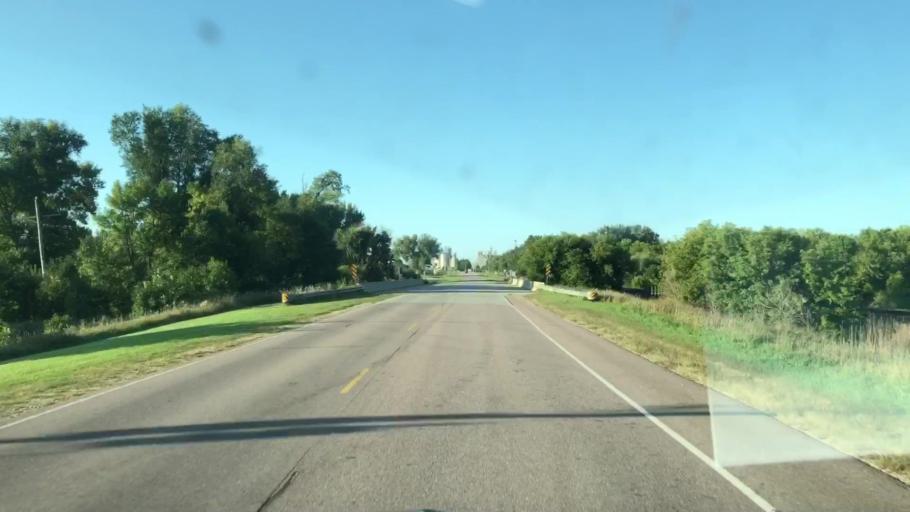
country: US
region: Iowa
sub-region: O'Brien County
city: Sheldon
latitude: 43.1971
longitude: -95.8485
